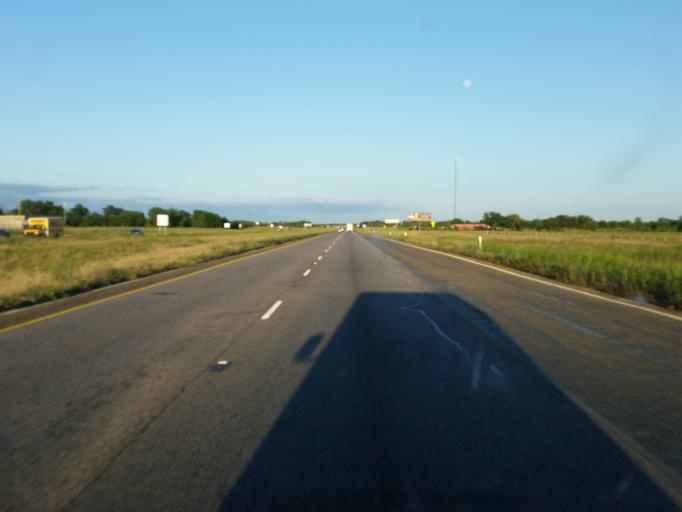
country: US
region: Texas
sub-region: Van Zandt County
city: Wills Point
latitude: 32.6543
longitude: -96.0905
